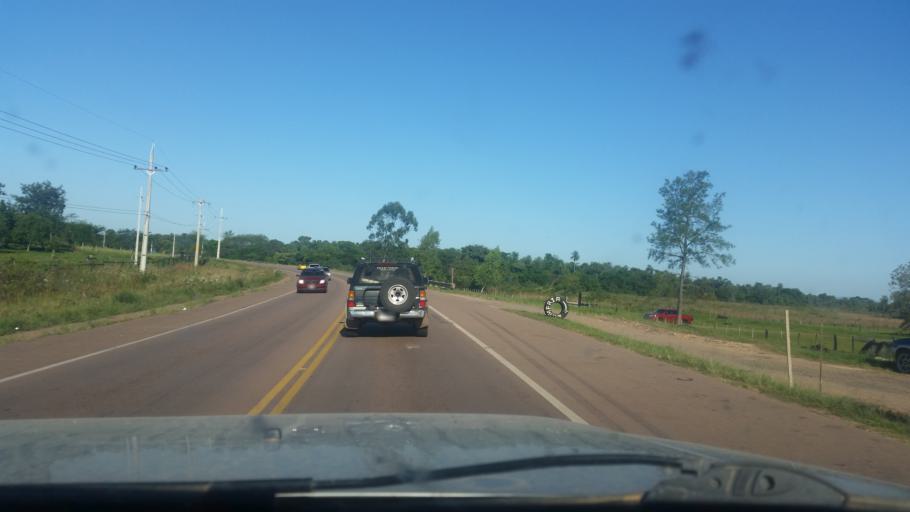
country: PY
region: Paraguari
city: Paraguari
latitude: -25.6347
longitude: -57.0636
